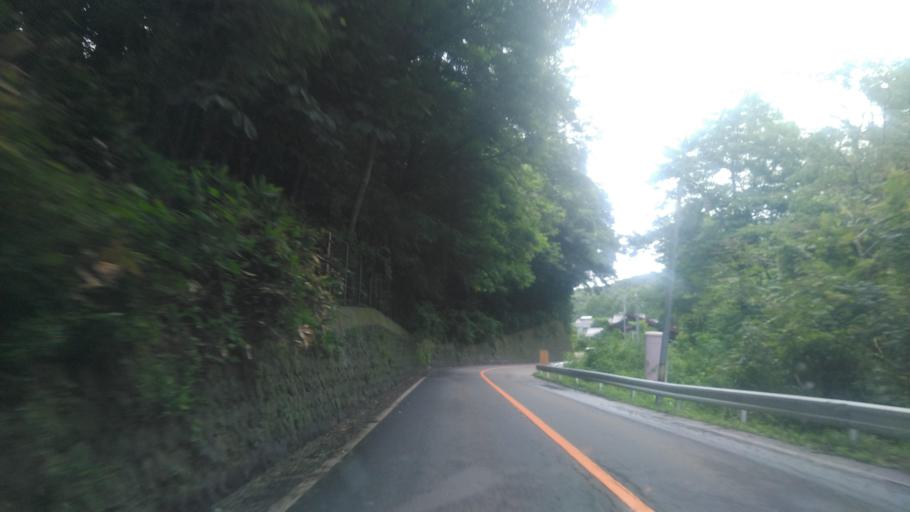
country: JP
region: Nagano
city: Ueda
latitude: 36.4887
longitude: 138.3800
